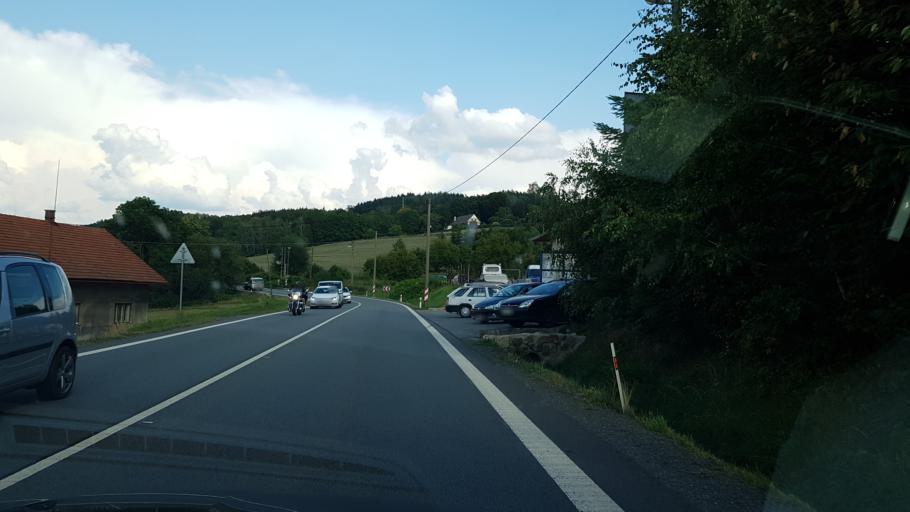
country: CZ
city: Vamberk
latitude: 50.1191
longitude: 16.3062
